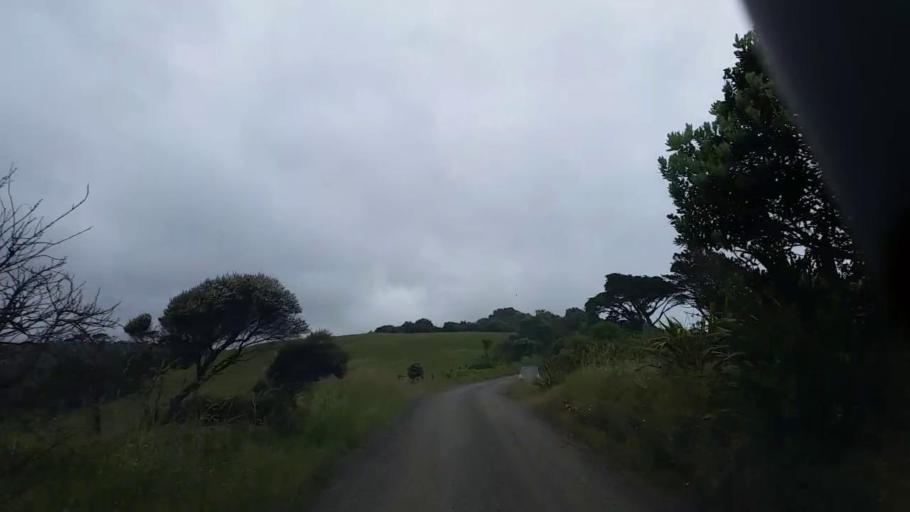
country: NZ
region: Auckland
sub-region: Auckland
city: Muriwai Beach
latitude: -36.9262
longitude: 174.4589
